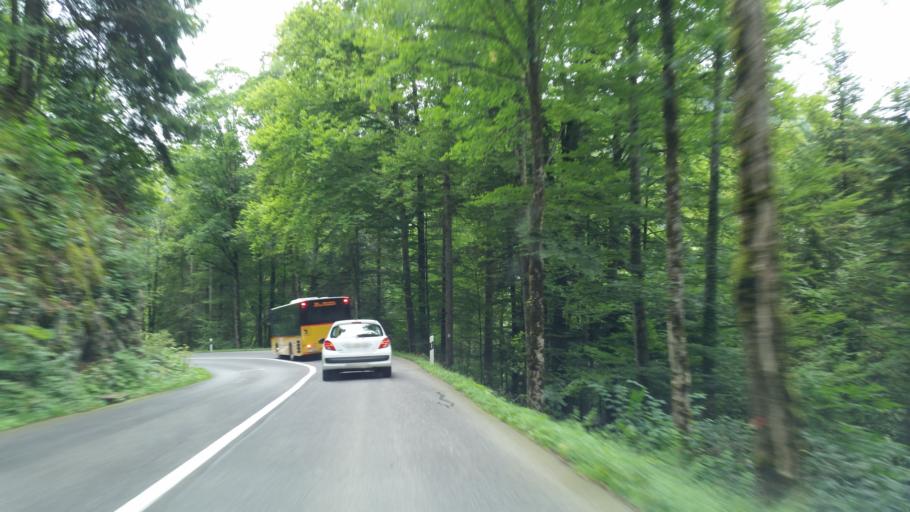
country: CH
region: Neuchatel
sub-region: La Chaux-de-Fonds District
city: La Chaux-de-Fonds
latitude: 47.1475
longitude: 6.8403
